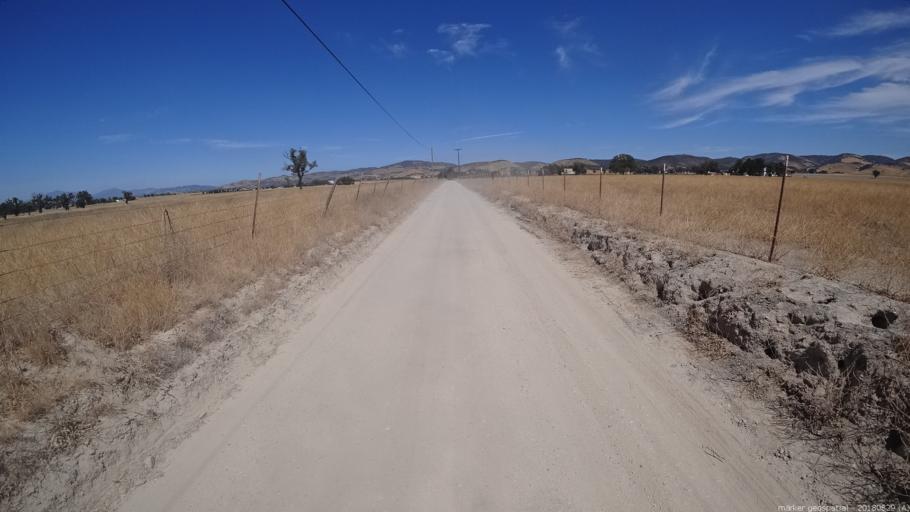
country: US
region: California
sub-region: Monterey County
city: King City
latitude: 35.9371
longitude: -121.0732
